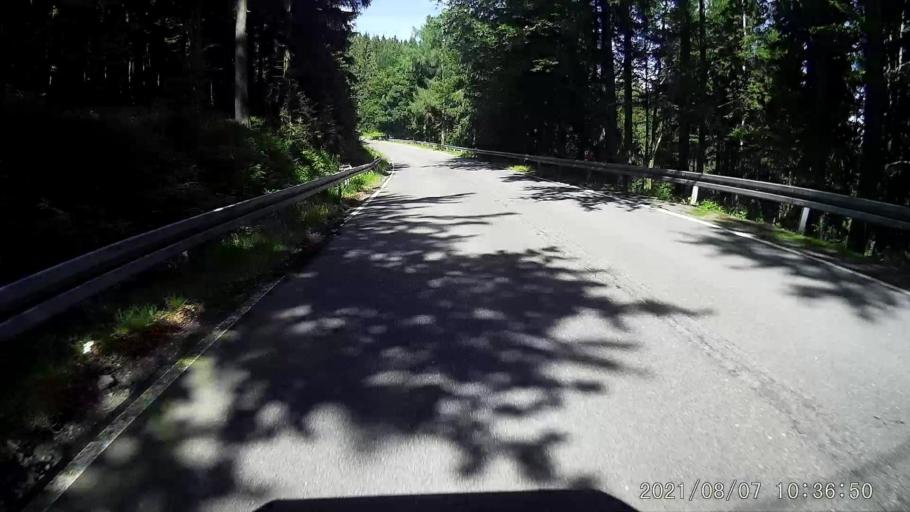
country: PL
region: Lower Silesian Voivodeship
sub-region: Powiat klodzki
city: Duszniki-Zdroj
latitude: 50.3600
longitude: 16.3728
